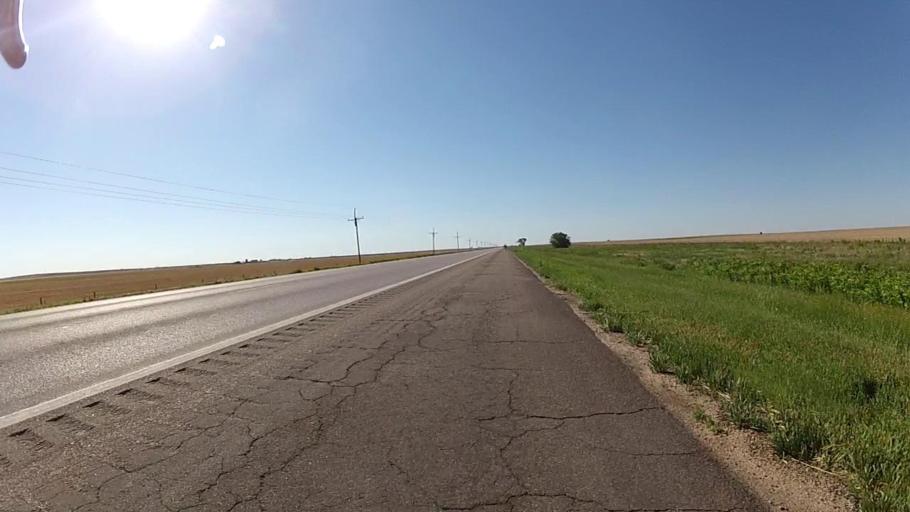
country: US
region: Kansas
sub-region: Ford County
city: Dodge City
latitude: 37.5977
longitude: -99.6976
